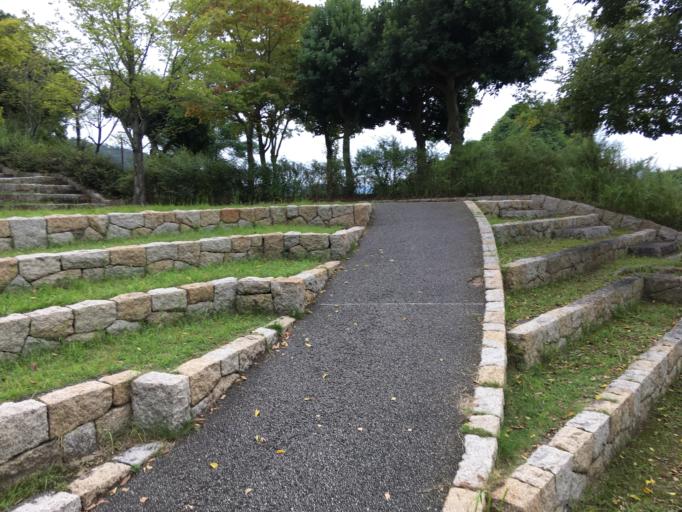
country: JP
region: Nara
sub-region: Ikoma-shi
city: Ikoma
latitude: 34.6229
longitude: 135.7008
